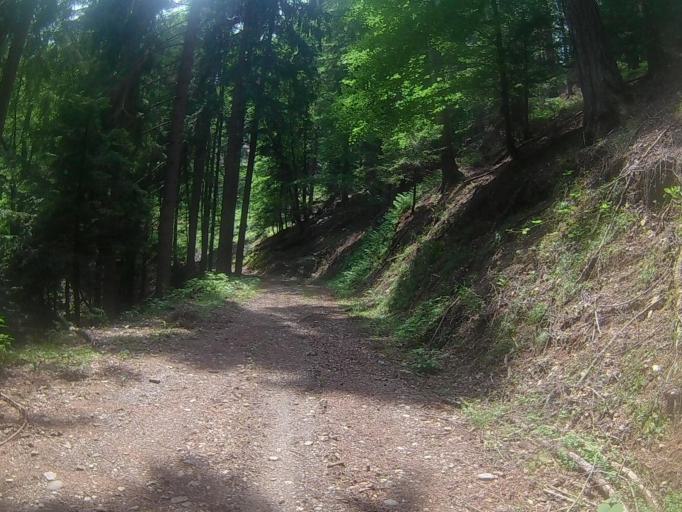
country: SI
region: Ruse
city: Ruse
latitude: 46.5157
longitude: 15.5448
